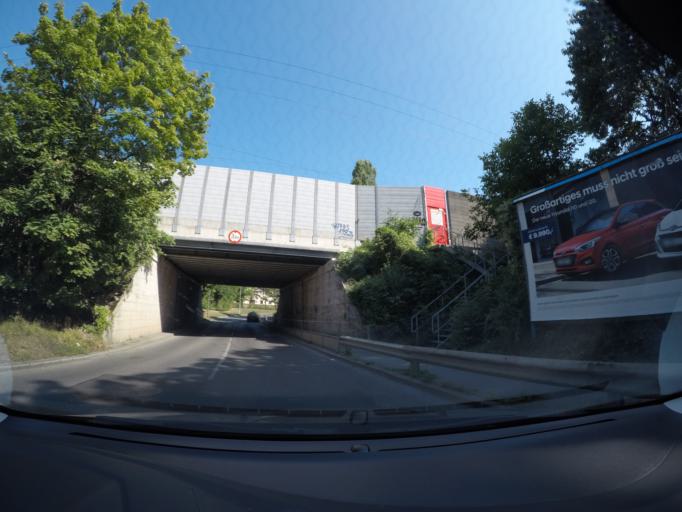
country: AT
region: Lower Austria
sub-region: Politischer Bezirk Modling
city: Perchtoldsdorf
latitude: 48.1453
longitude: 16.2872
